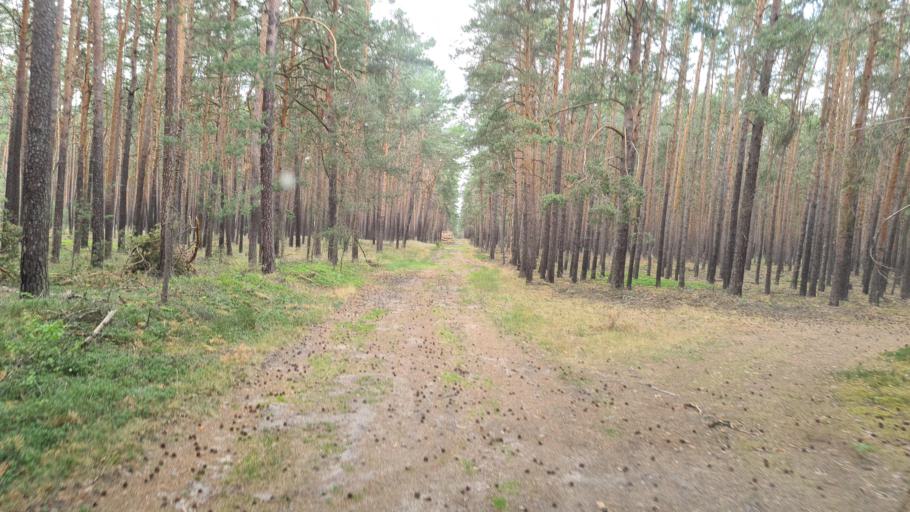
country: DE
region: Brandenburg
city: Crinitz
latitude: 51.6783
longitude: 13.7537
